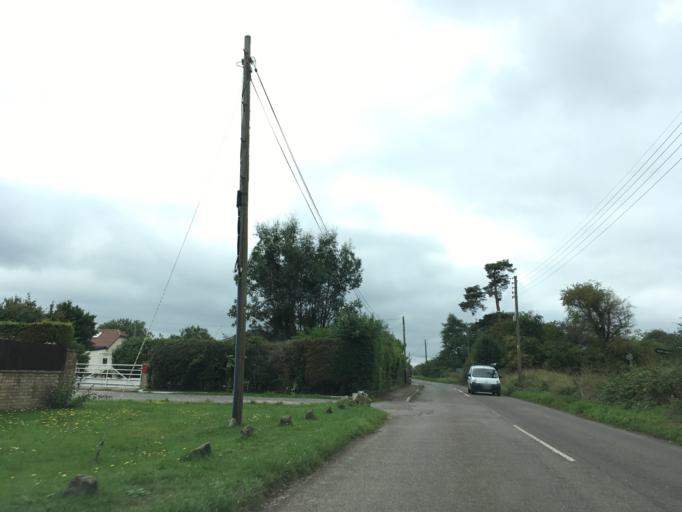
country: GB
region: England
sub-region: South Gloucestershire
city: Siston
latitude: 51.4644
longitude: -2.4592
